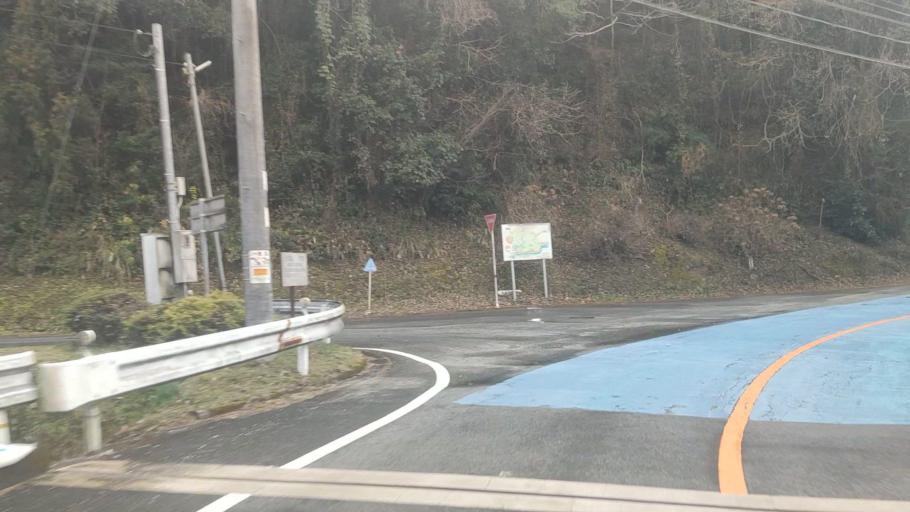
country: JP
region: Kumamoto
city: Hitoyoshi
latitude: 32.2888
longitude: 130.8464
